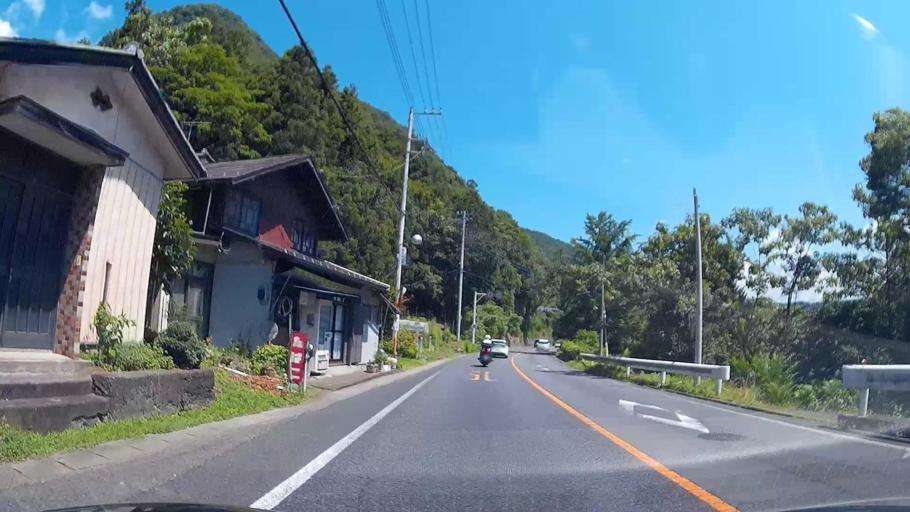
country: JP
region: Gunma
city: Numata
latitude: 36.5679
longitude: 139.0380
